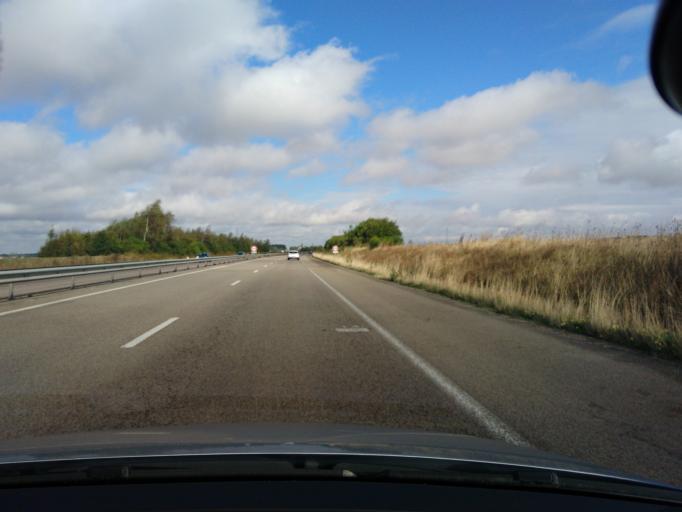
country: FR
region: Haute-Normandie
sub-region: Departement de l'Eure
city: Damville
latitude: 48.8941
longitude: 1.1716
